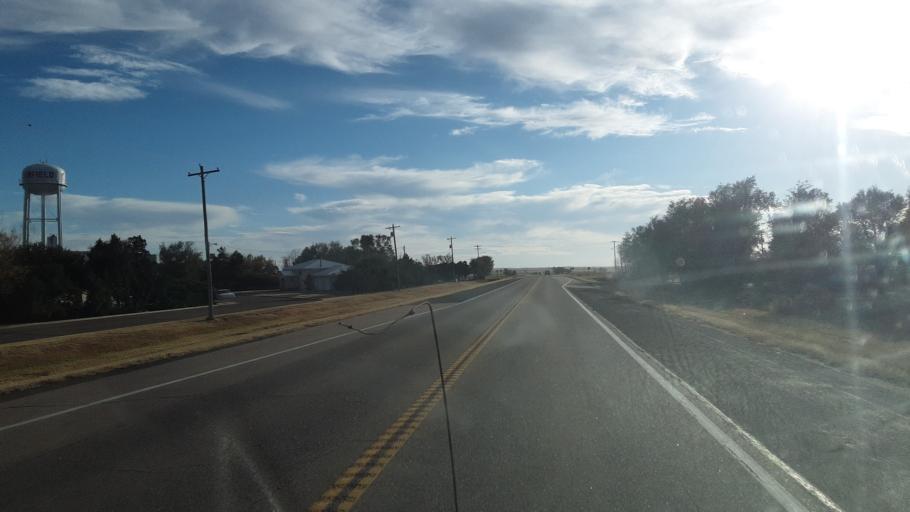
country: US
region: Kansas
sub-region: Kearny County
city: Lakin
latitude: 37.9854
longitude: -101.1376
